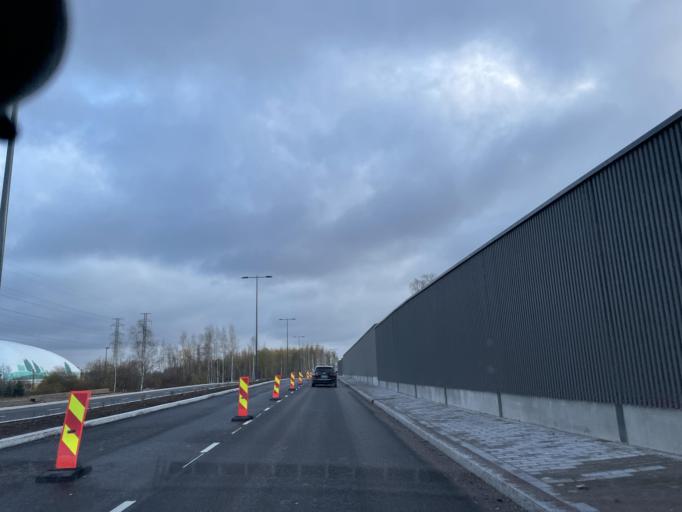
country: FI
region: Uusimaa
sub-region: Helsinki
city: Kauniainen
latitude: 60.1725
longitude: 24.6951
